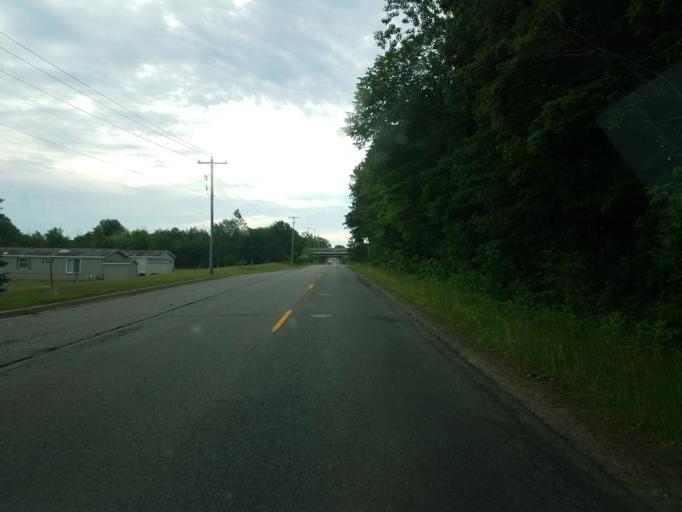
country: US
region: Michigan
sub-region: Eaton County
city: Charlotte
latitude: 42.5821
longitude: -84.8204
